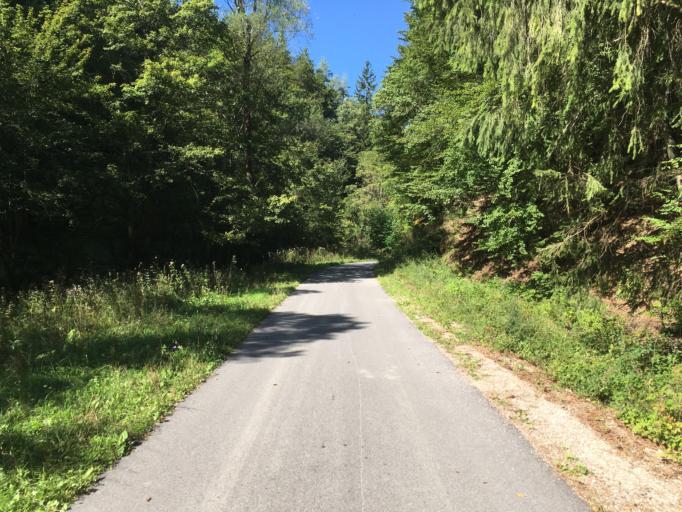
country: SK
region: Trenciansky
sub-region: Okres Povazska Bystrica
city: Povazska Bystrica
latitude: 49.0148
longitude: 18.4408
